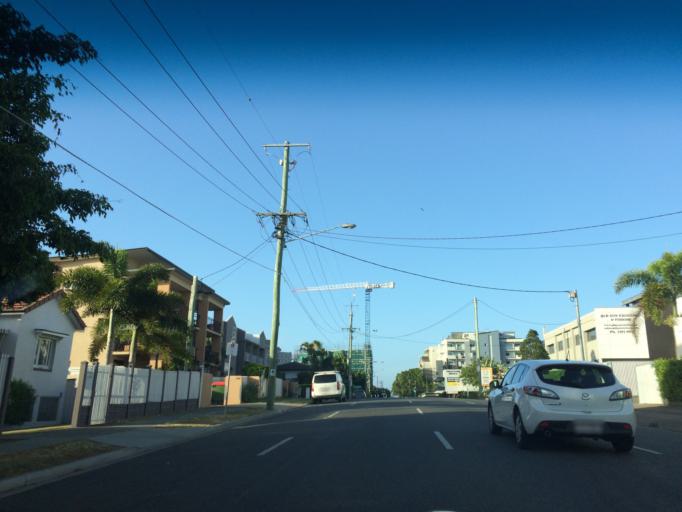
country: AU
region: Queensland
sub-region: Brisbane
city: Woolloongabba
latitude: -27.4806
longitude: 153.0411
